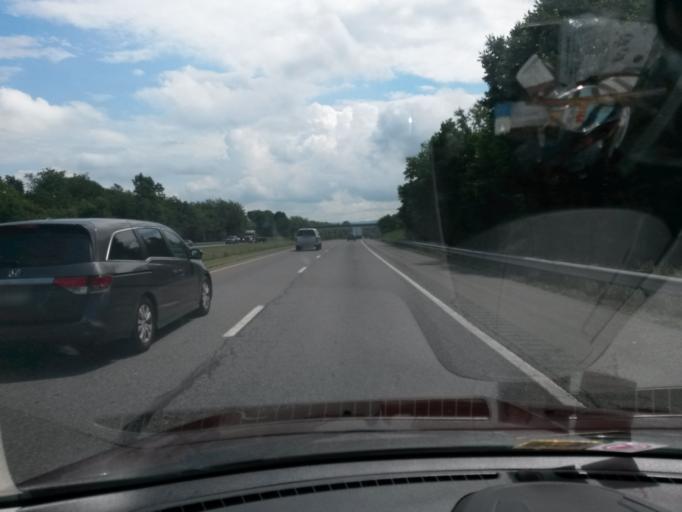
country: US
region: North Carolina
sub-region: Surry County
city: Elkin
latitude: 36.3264
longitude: -80.7949
